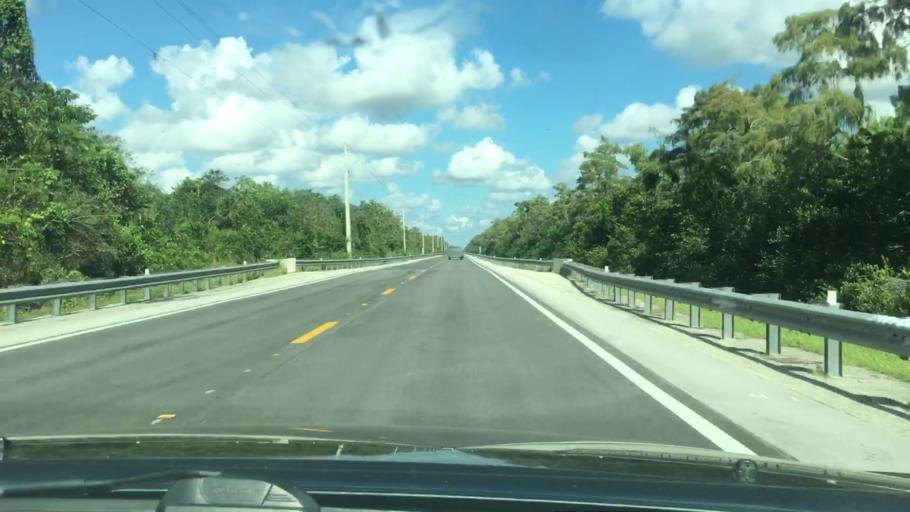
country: US
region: Florida
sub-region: Miami-Dade County
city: Kendall West
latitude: 25.7693
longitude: -80.8358
